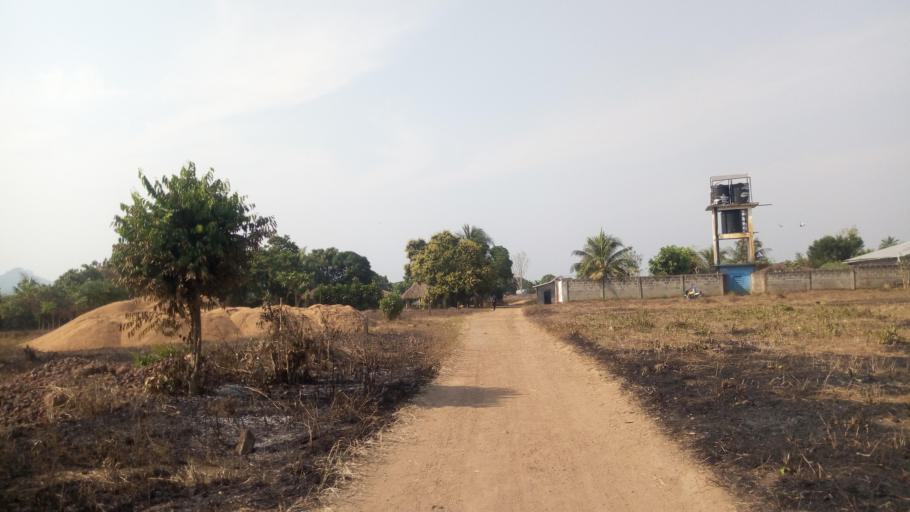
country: SL
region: Southern Province
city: Mogbwemo
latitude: 7.6158
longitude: -12.1797
